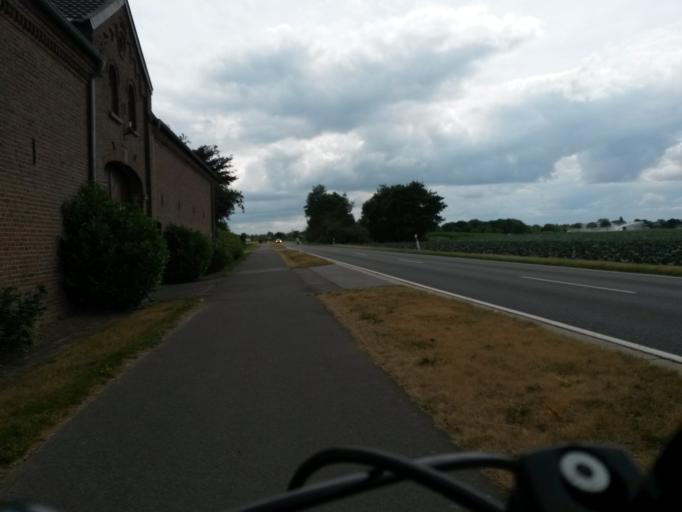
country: DE
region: North Rhine-Westphalia
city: Kempen
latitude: 51.3652
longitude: 6.3940
